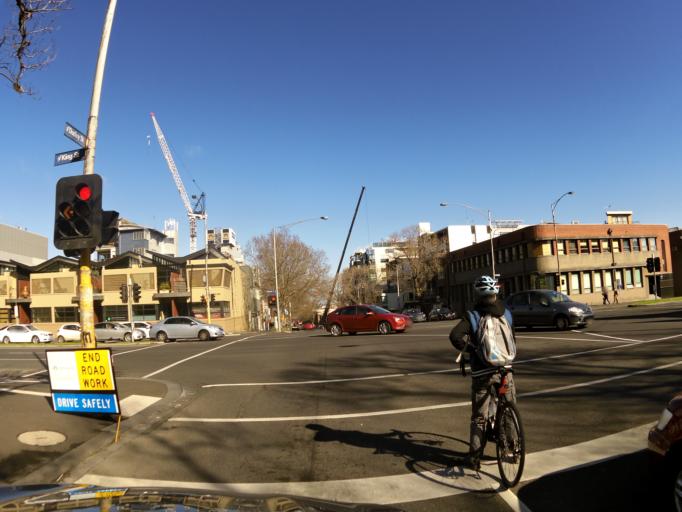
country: AU
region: Victoria
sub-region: Melbourne
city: West Melbourne
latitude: -37.8092
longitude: 144.9527
